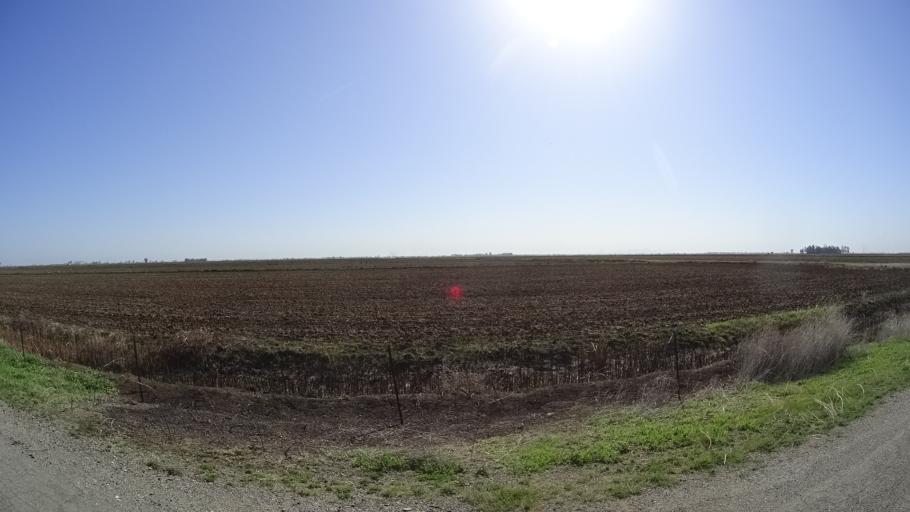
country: US
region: California
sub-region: Glenn County
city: Willows
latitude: 39.4410
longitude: -122.2305
